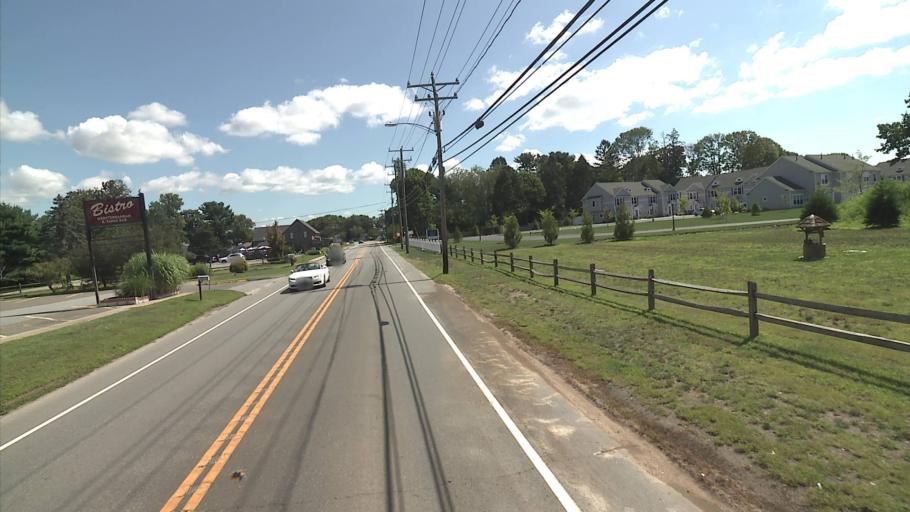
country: US
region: Connecticut
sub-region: Middlesex County
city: Westbrook Center
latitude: 41.2787
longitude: -72.4633
